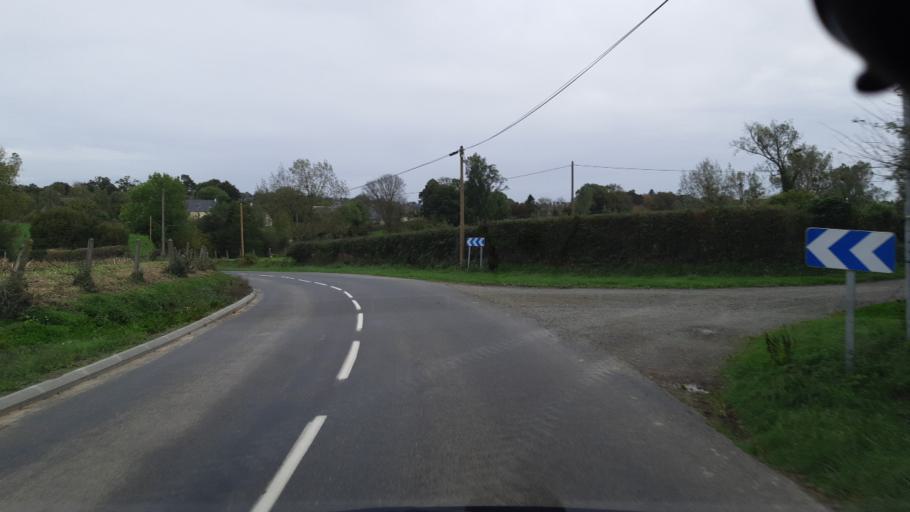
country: FR
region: Lower Normandy
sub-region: Departement de la Manche
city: Hambye
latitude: 48.9535
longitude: -1.2662
